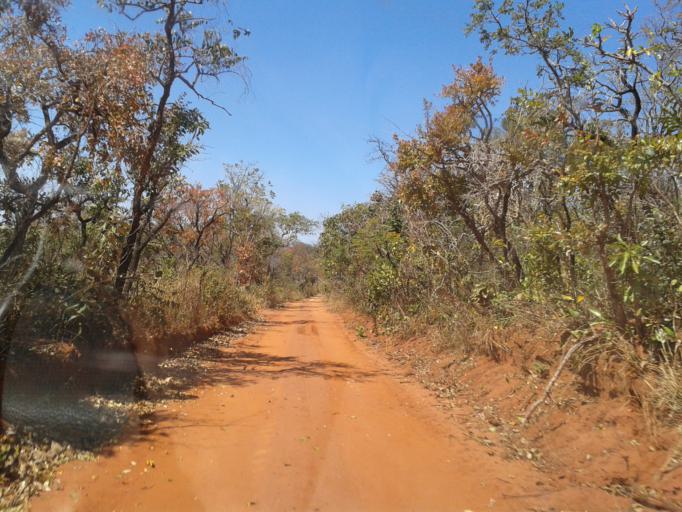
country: BR
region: Minas Gerais
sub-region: Monte Alegre De Minas
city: Monte Alegre de Minas
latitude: -18.8358
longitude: -49.0959
